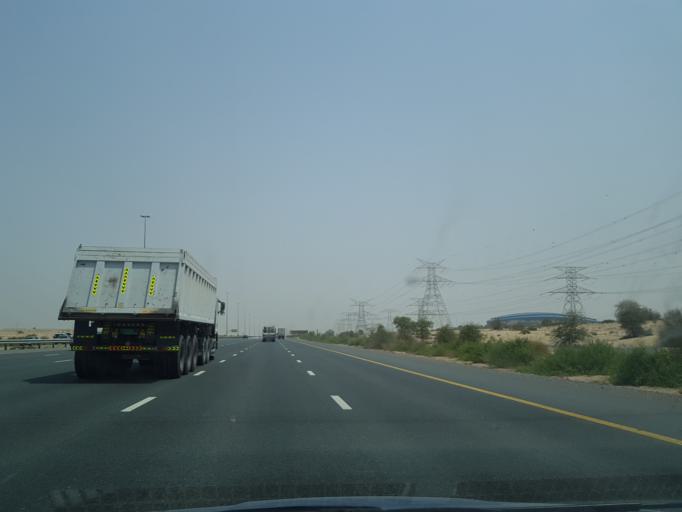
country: AE
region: Dubai
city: Dubai
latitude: 25.0470
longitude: 55.3081
